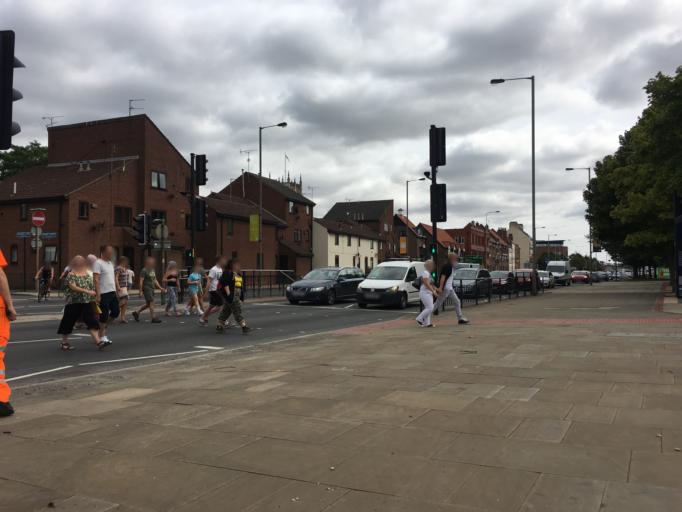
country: GB
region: England
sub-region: City of Kingston upon Hull
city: Hull
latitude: 53.7408
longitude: -0.3376
